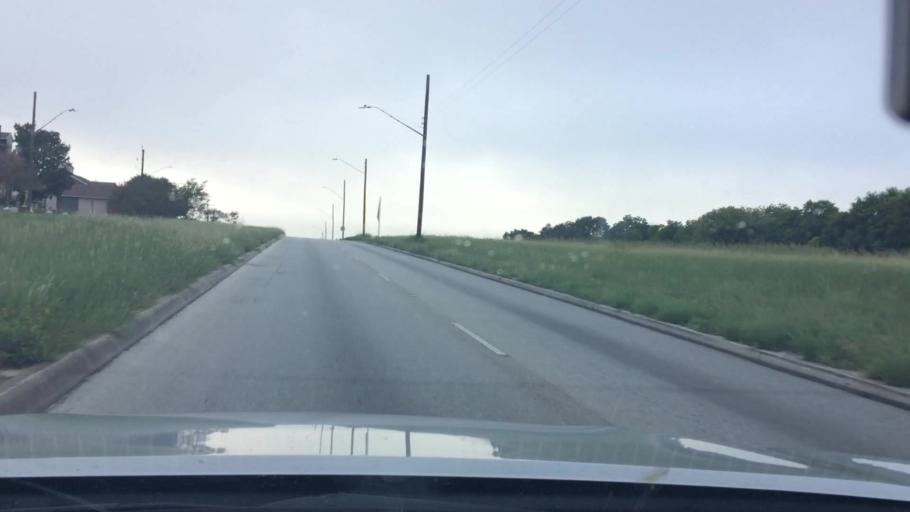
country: US
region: Texas
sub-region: Bexar County
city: Windcrest
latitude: 29.5443
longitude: -98.3996
